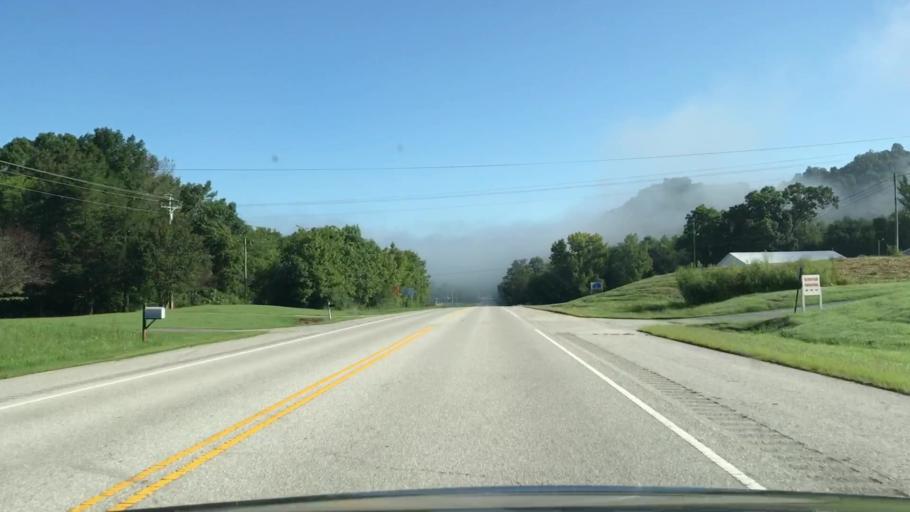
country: US
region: Tennessee
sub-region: Jackson County
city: Gainesboro
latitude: 36.3866
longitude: -85.6367
